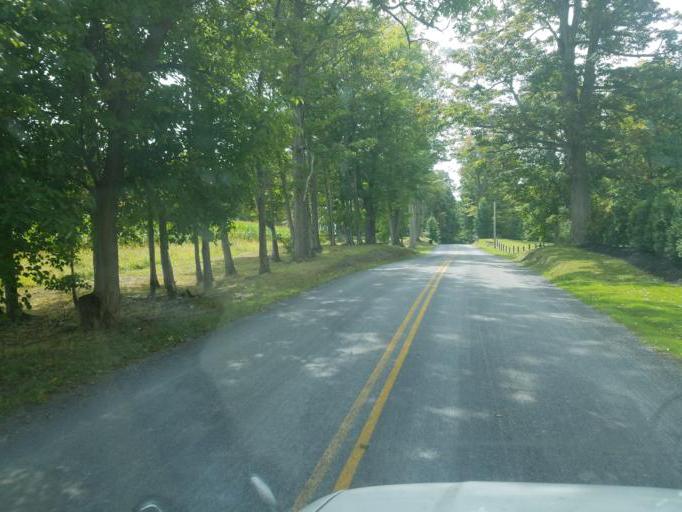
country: US
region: Ohio
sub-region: Geauga County
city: Middlefield
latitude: 41.4335
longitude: -80.9730
